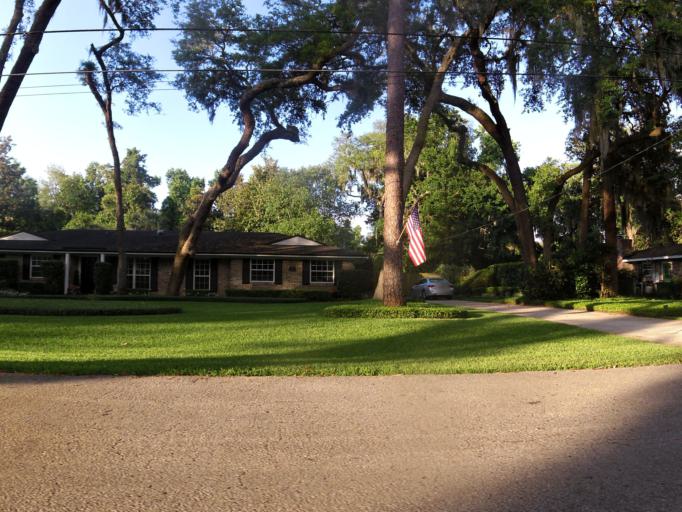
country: US
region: Florida
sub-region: Clay County
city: Orange Park
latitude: 30.2115
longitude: -81.6233
